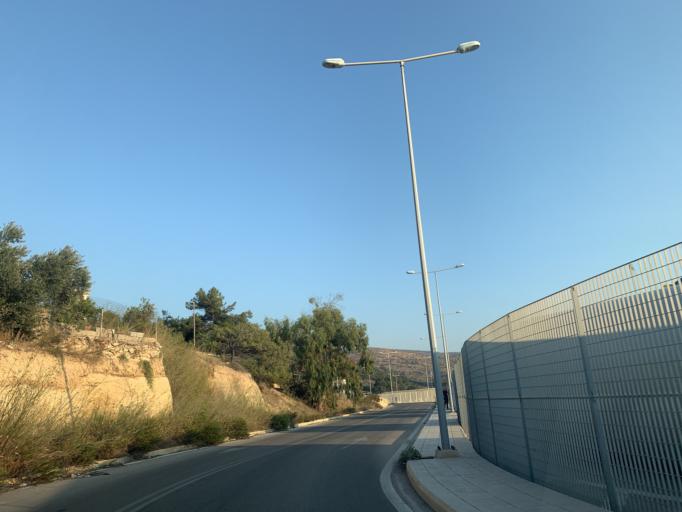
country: GR
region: North Aegean
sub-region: Chios
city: Thymiana
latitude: 38.2906
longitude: 25.9304
